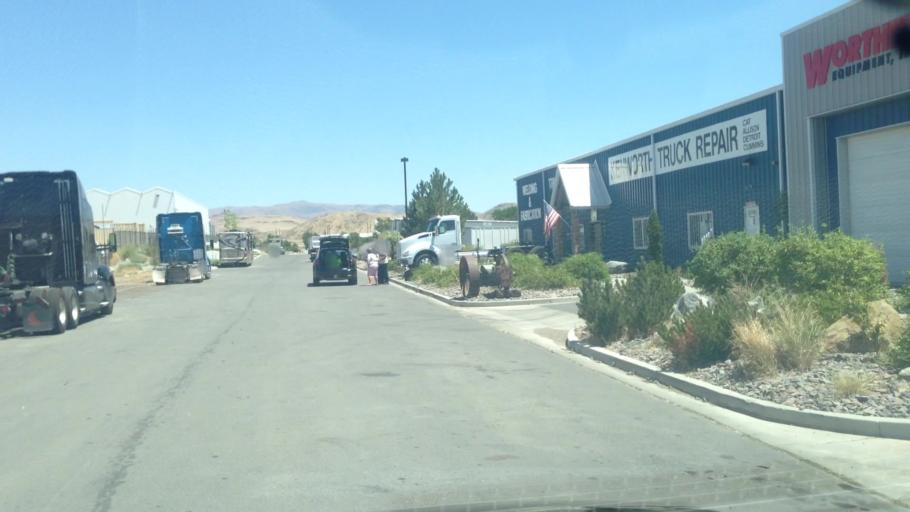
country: US
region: Nevada
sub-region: Washoe County
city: Sparks
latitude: 39.5180
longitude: -119.6274
